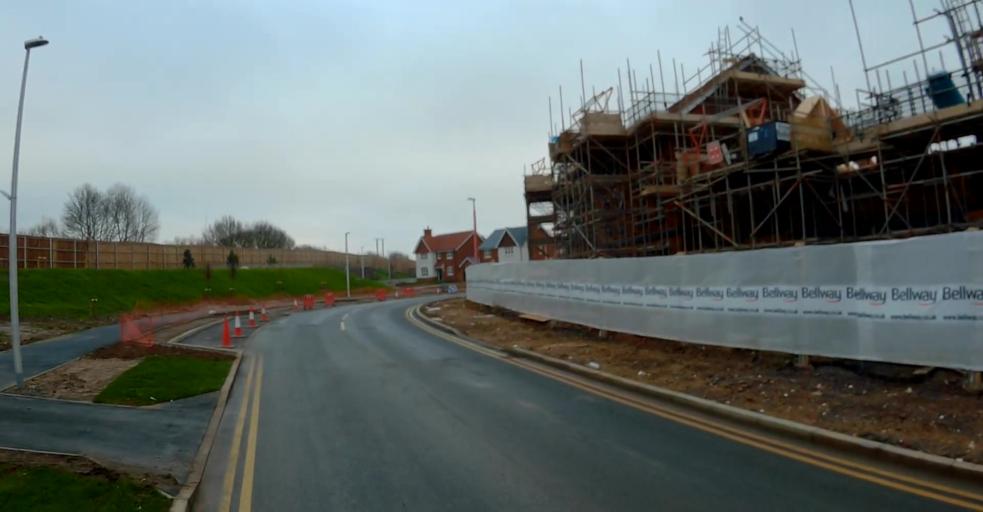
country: GB
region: England
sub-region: Bracknell Forest
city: Binfield
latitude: 51.4160
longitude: -0.8066
